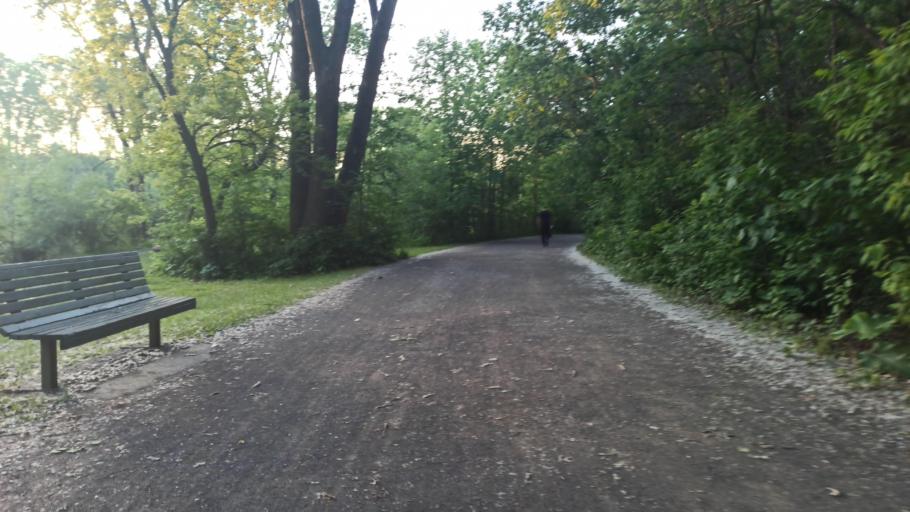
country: CA
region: Quebec
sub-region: Laval
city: Laval
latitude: 45.5768
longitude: -73.6605
